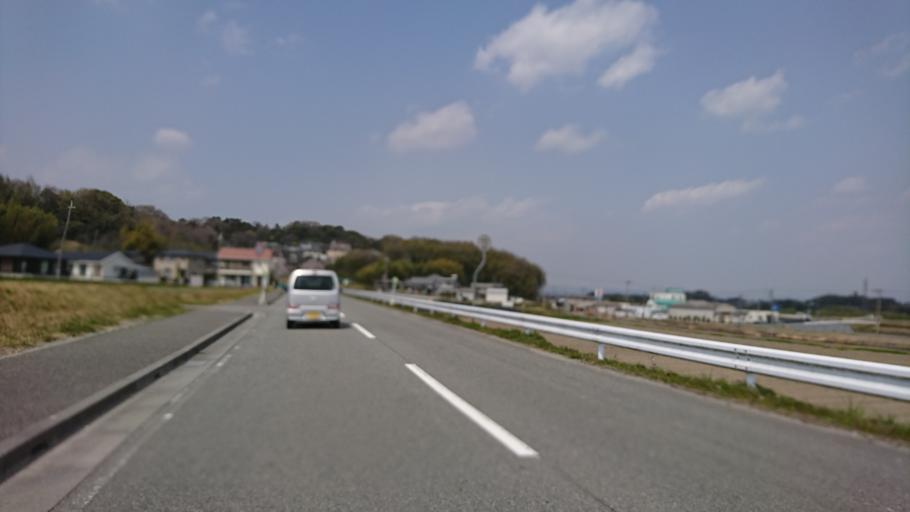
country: JP
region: Hyogo
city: Ono
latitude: 34.8399
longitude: 134.9104
